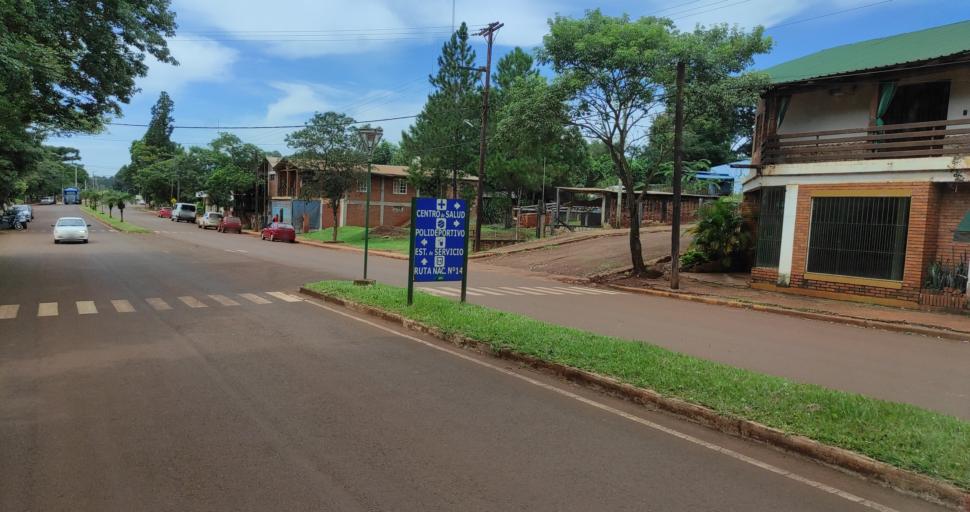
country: AR
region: Misiones
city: El Alcazar
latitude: -26.7142
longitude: -54.8145
